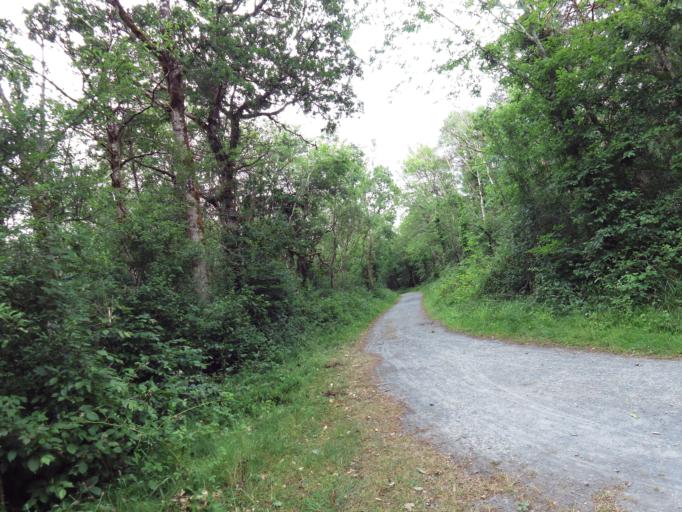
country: IE
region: Connaught
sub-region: County Galway
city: Gort
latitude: 53.0794
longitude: -8.8688
